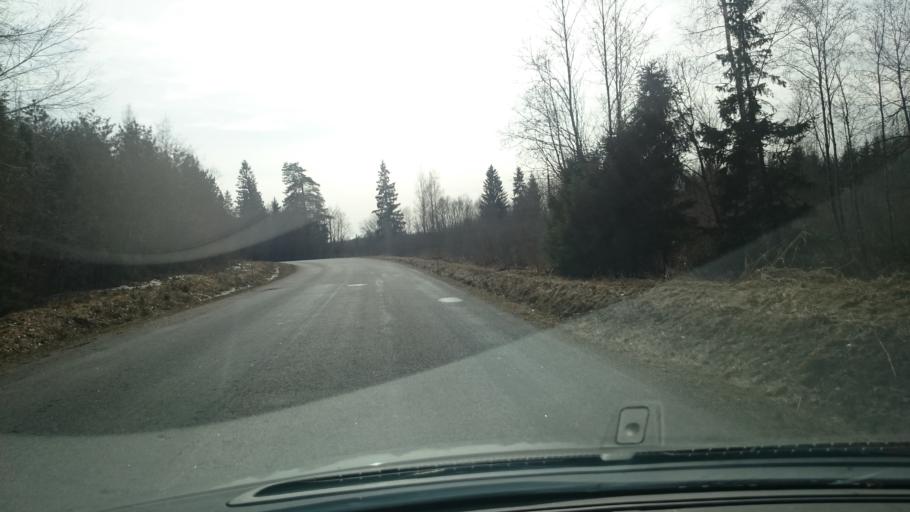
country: EE
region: Jaervamaa
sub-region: Paide linn
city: Paide
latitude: 58.9321
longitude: 25.4434
